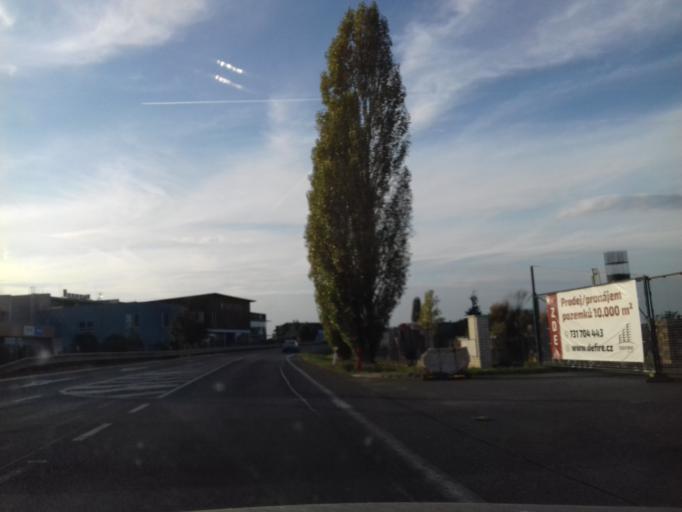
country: CZ
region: Central Bohemia
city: Vestec
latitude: 49.9715
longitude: 14.5049
